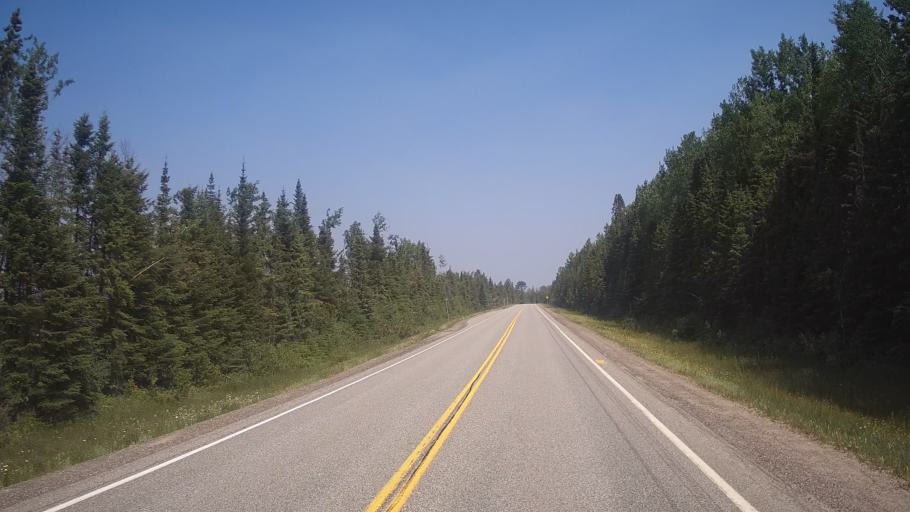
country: CA
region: Ontario
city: Timmins
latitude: 48.0477
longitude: -81.5836
